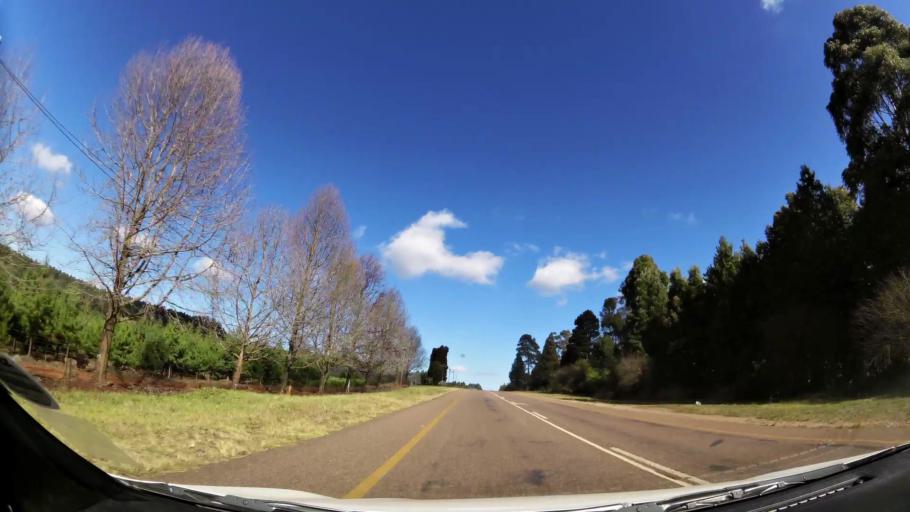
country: ZA
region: Limpopo
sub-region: Capricorn District Municipality
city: Mankoeng
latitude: -23.8974
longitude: 29.9937
